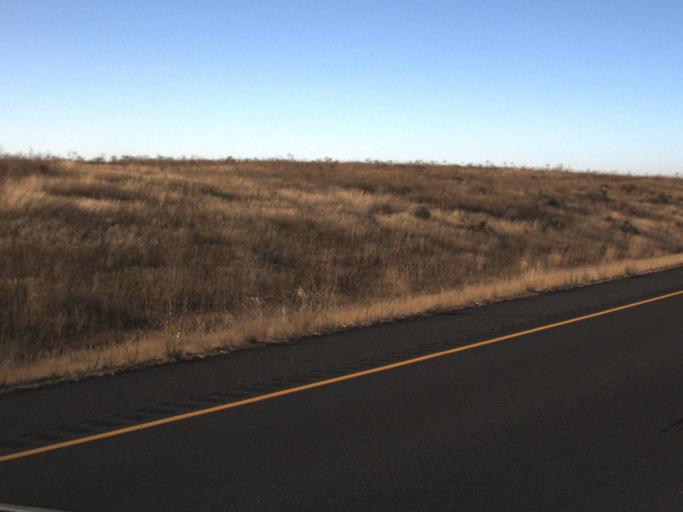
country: US
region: Washington
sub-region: Franklin County
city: Connell
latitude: 46.5921
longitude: -118.9601
